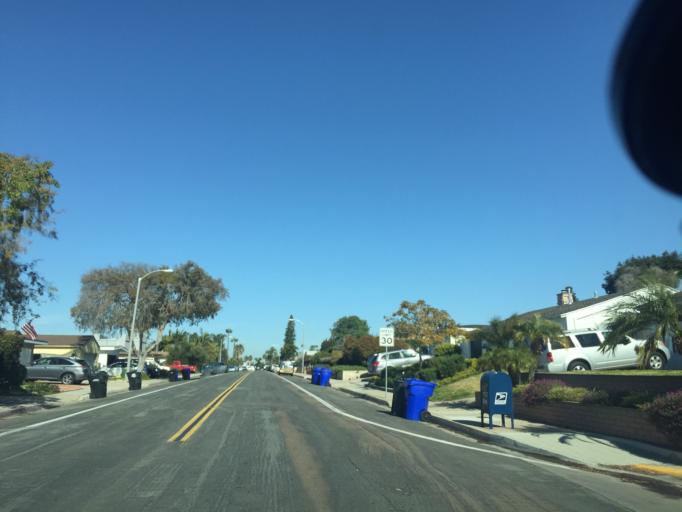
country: US
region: California
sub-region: San Diego County
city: San Diego
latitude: 32.7906
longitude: -117.1924
